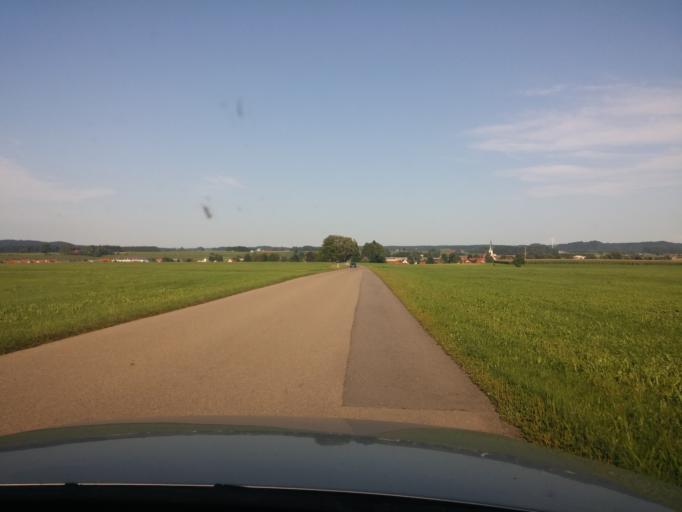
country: DE
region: Bavaria
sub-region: Swabia
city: Legau
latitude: 47.8566
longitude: 10.1157
